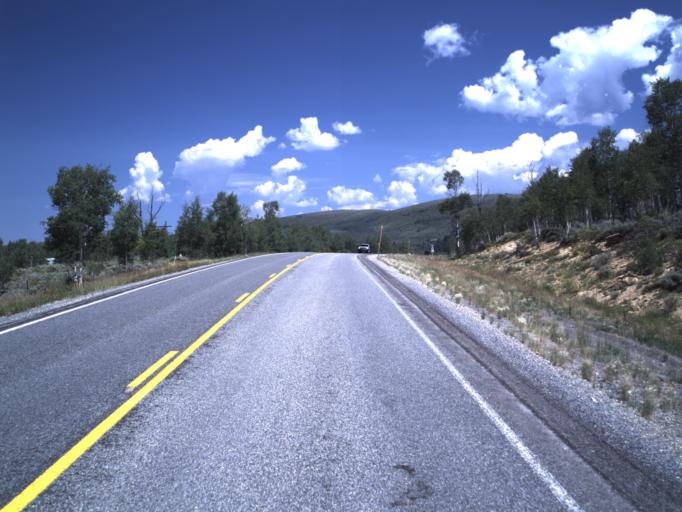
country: US
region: Utah
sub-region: Carbon County
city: Helper
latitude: 39.8519
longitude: -111.1274
